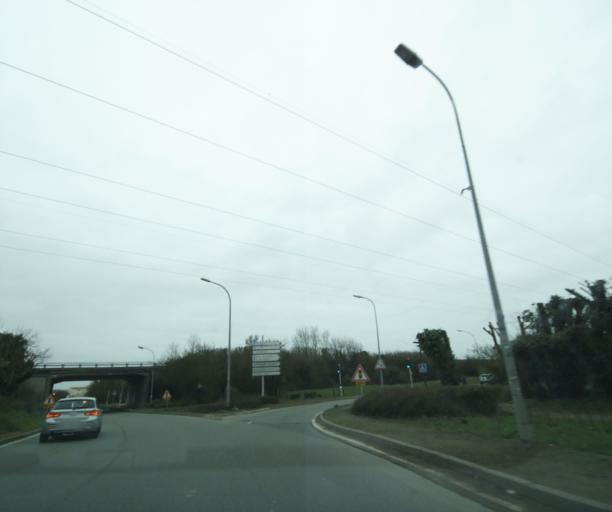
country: FR
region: Poitou-Charentes
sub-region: Departement de la Charente-Maritime
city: Lagord
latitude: 46.1801
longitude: -1.1534
